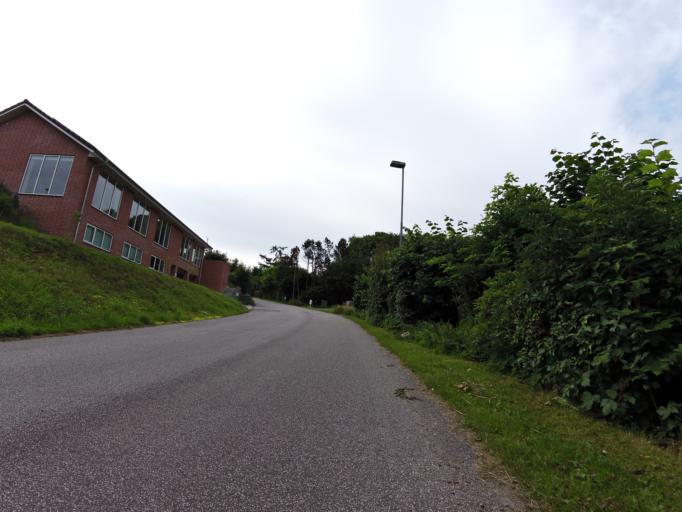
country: DK
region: Central Jutland
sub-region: Arhus Kommune
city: Kolt
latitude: 56.1262
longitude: 10.0562
